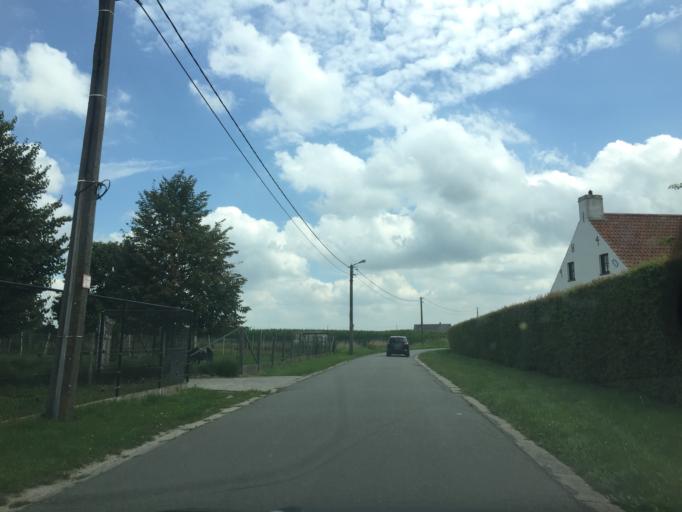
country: BE
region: Flanders
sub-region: Provincie West-Vlaanderen
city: Lichtervelde
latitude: 51.0392
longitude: 3.1294
